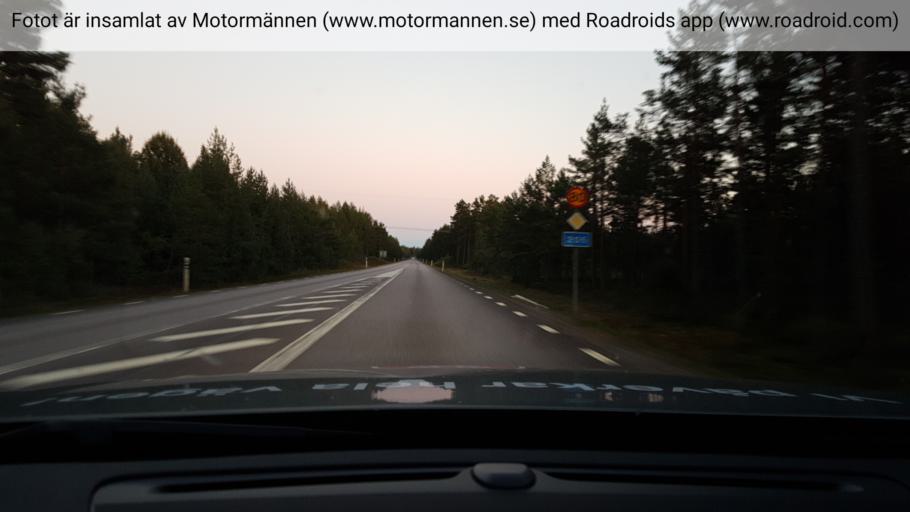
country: SE
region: OErebro
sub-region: Laxa Kommun
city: Laxa
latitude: 58.9415
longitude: 14.6354
